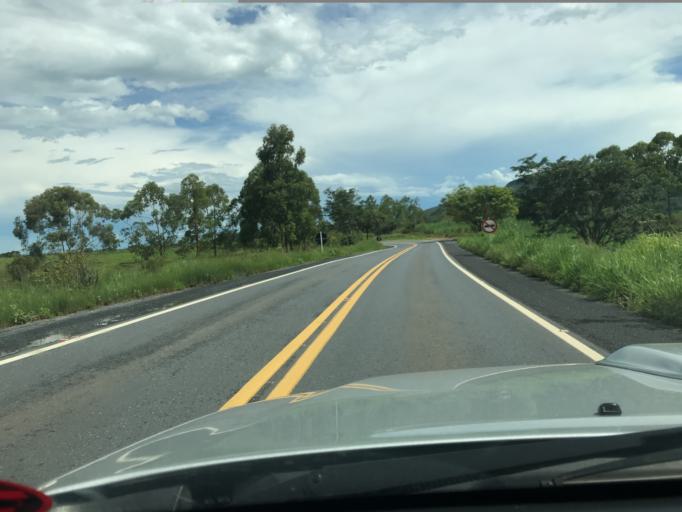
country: BR
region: Minas Gerais
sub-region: Campos Altos
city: Campos Altos
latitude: -19.8086
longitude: -46.0328
